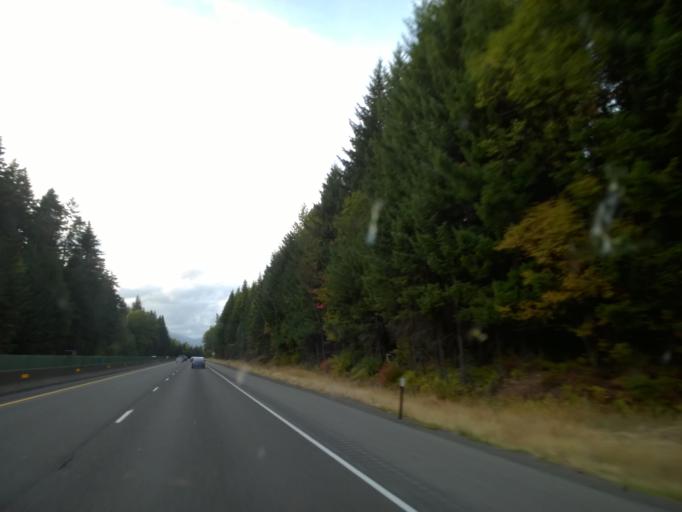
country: US
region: Washington
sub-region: Kittitas County
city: Cle Elum
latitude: 47.2744
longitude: -121.2743
